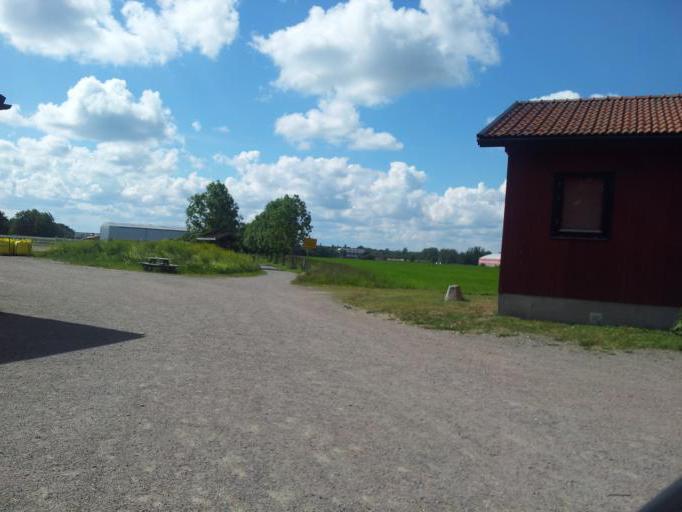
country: SE
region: Uppsala
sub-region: Uppsala Kommun
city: Uppsala
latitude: 59.8798
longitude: 17.6681
